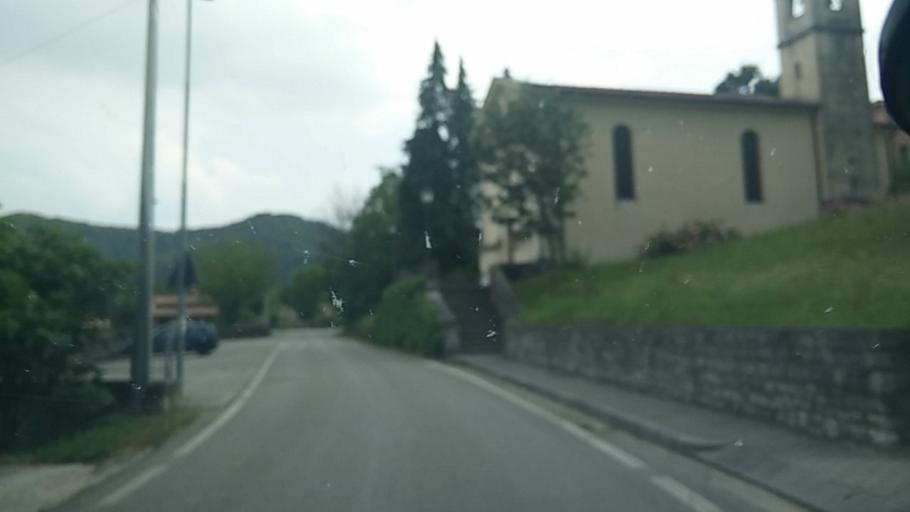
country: IT
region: Veneto
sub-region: Provincia di Treviso
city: Follina
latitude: 45.9363
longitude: 12.1259
